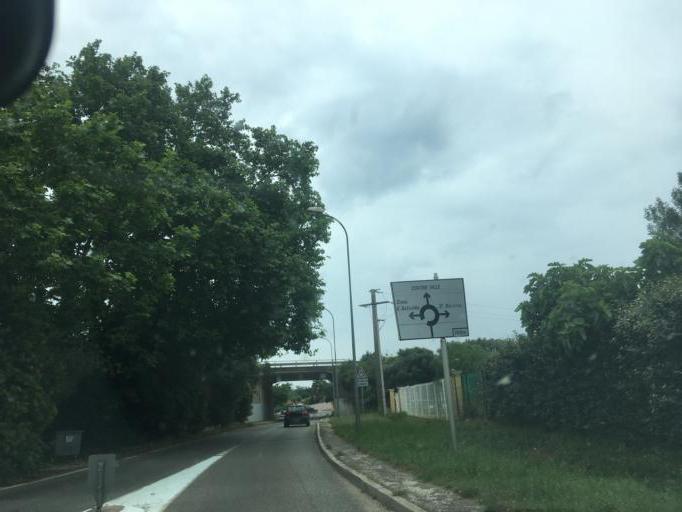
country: FR
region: Provence-Alpes-Cote d'Azur
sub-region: Departement du Var
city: La Londe-les-Maures
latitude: 43.1445
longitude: 6.2296
